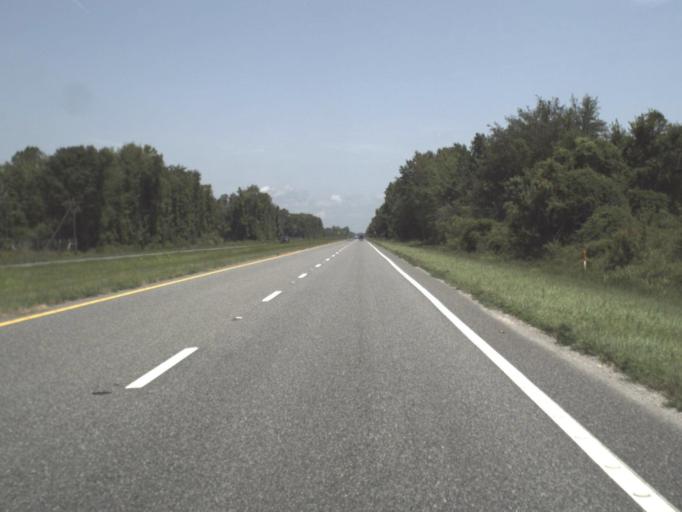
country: US
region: Florida
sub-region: Taylor County
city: Steinhatchee
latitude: 29.8326
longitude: -83.3631
